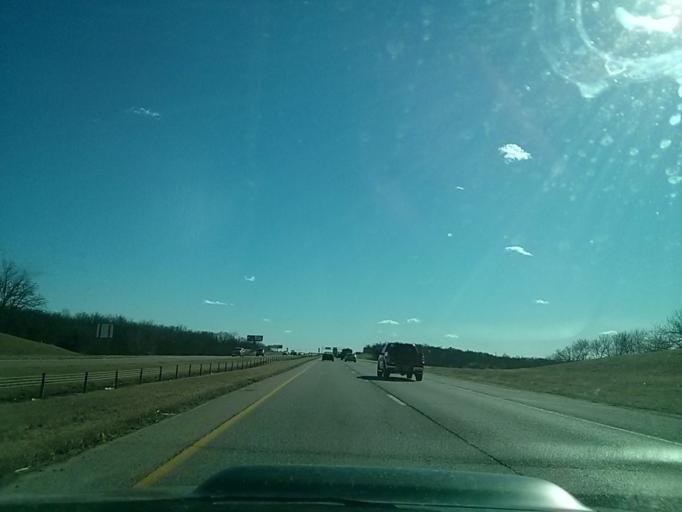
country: US
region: Oklahoma
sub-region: Tulsa County
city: Oakhurst
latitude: 36.0736
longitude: -96.0067
